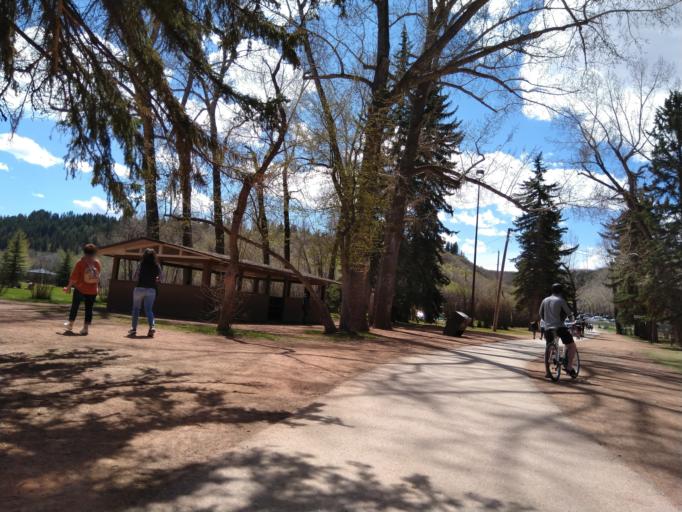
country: CA
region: Alberta
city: Calgary
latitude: 51.0634
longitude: -114.1545
